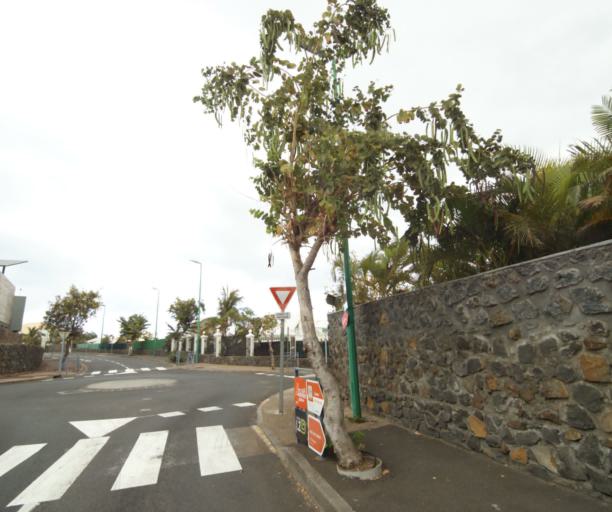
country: RE
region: Reunion
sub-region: Reunion
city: Saint-Paul
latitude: -21.0599
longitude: 55.2304
